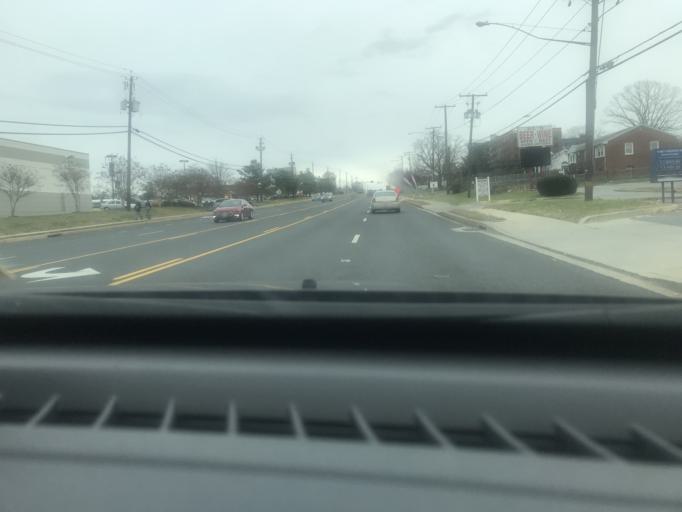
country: US
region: Maryland
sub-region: Prince George's County
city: Oxon Hill
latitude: 38.8037
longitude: -76.9861
